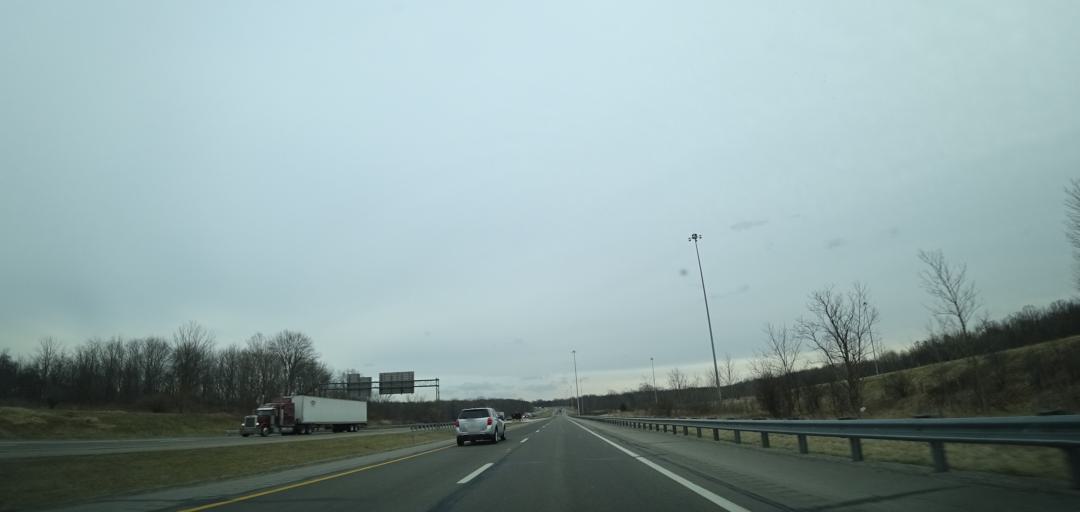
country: US
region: Ohio
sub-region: Mahoning County
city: Poland
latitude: 40.9541
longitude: -80.6380
